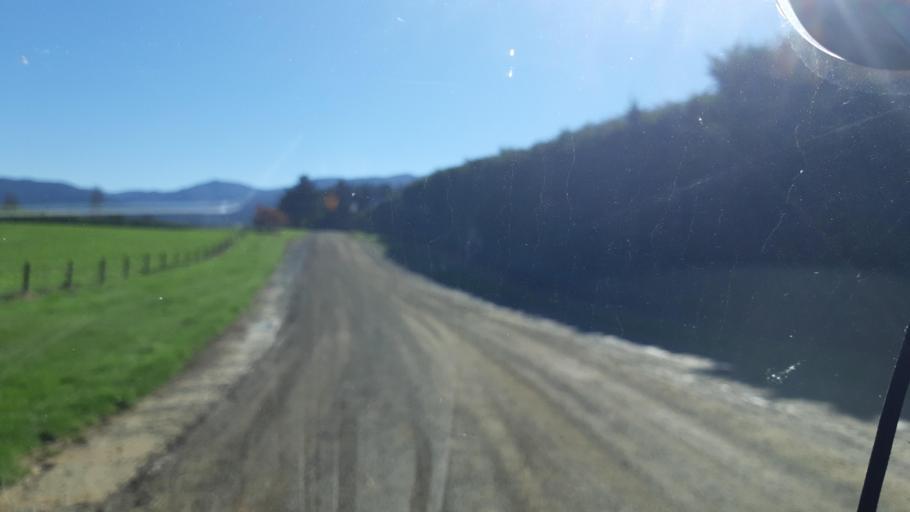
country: NZ
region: Canterbury
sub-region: Waimakariri District
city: Oxford
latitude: -43.2257
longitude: 172.3502
